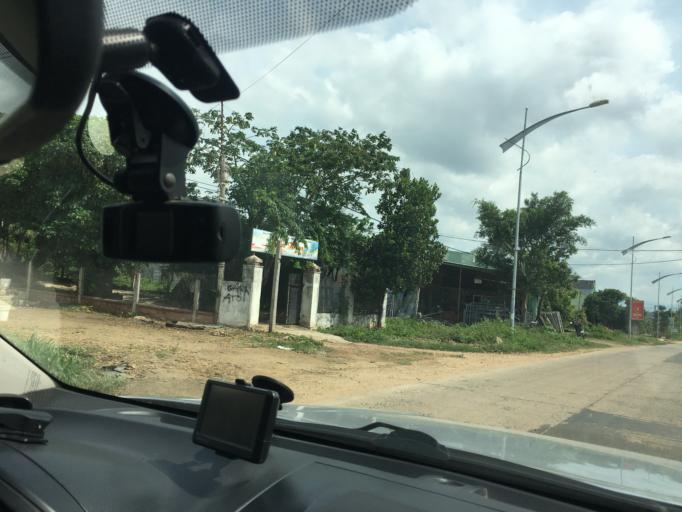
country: VN
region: Gia Lai
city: Kong Chro
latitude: 13.7820
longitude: 108.5181
